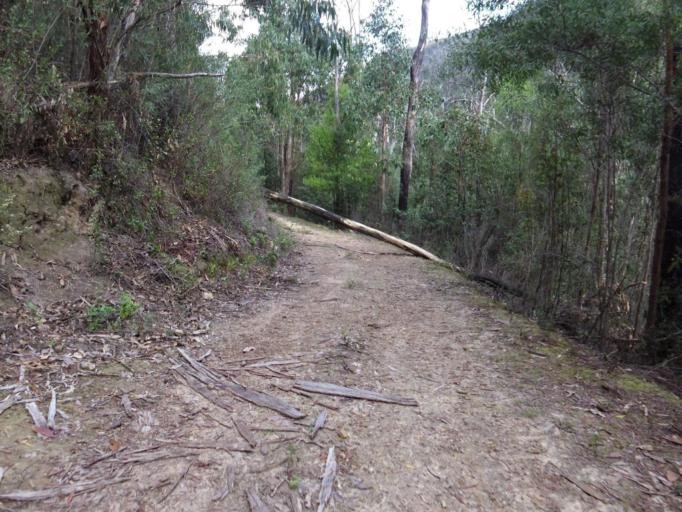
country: AU
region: Victoria
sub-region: Murrindindi
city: Kinglake West
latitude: -37.5157
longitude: 145.2352
